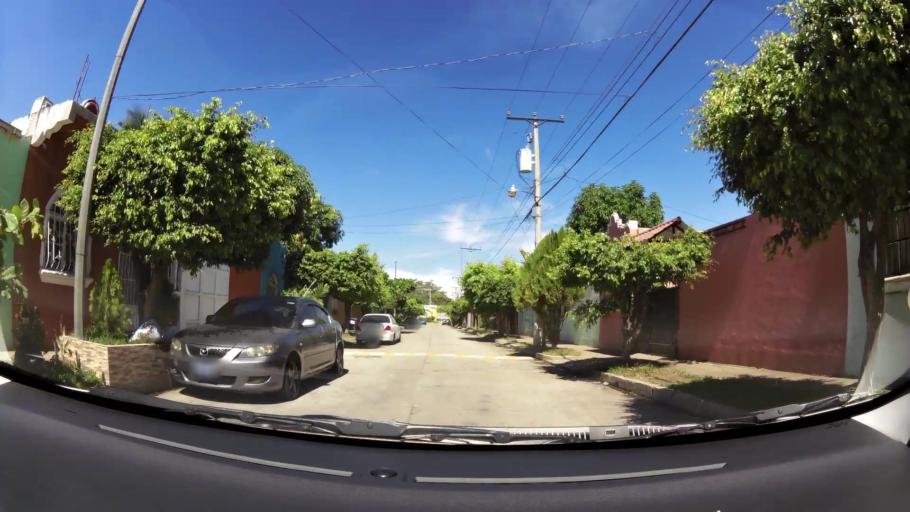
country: SV
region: La Libertad
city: San Juan Opico
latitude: 13.7972
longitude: -89.3575
